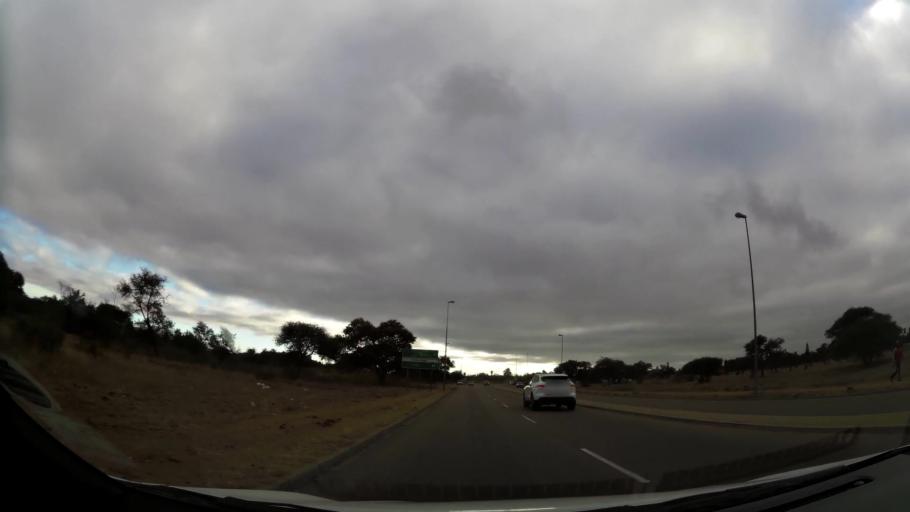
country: ZA
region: Limpopo
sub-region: Capricorn District Municipality
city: Polokwane
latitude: -23.8841
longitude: 29.4319
